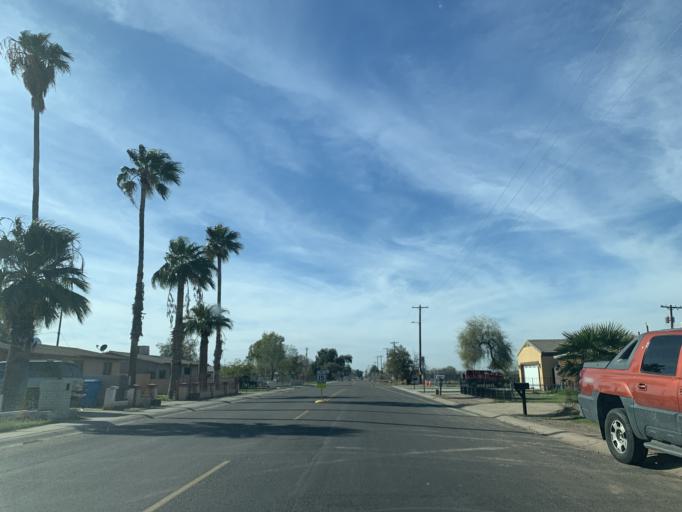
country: US
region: Arizona
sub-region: Maricopa County
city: Laveen
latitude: 33.4029
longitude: -112.1393
